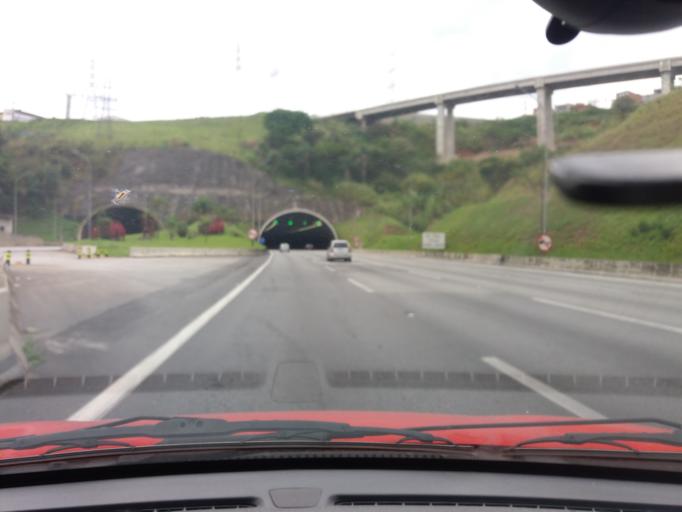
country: BR
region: Sao Paulo
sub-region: Carapicuiba
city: Carapicuiba
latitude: -23.4902
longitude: -46.8078
